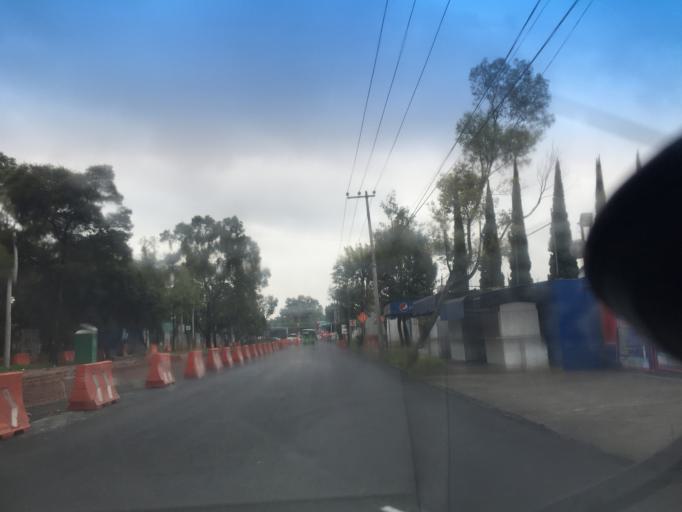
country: MX
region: Mexico City
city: Azcapotzalco
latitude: 19.5034
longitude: -99.1812
